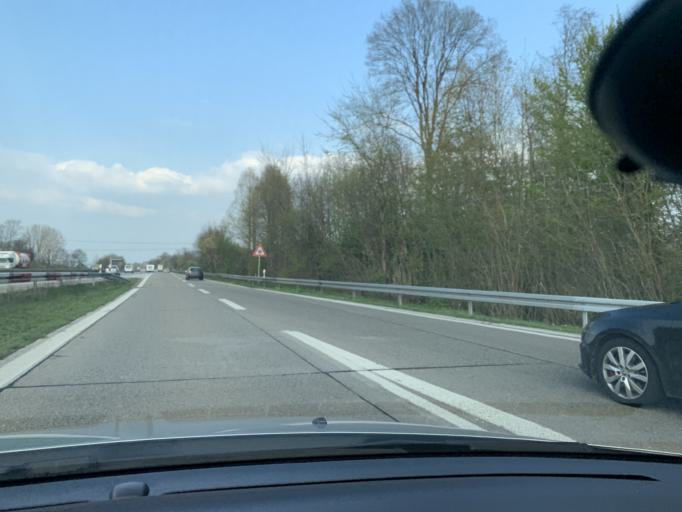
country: DE
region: Baden-Wuerttemberg
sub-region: Freiburg Region
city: Umkirch
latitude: 48.0250
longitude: 7.7872
